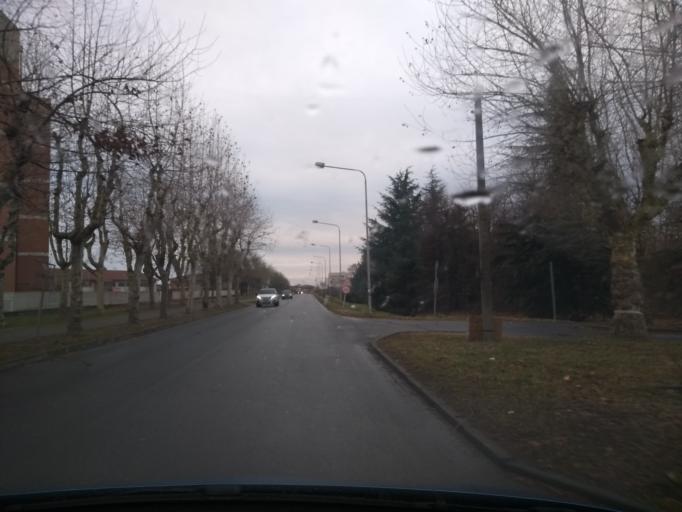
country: IT
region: Piedmont
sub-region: Provincia di Torino
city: Castellamonte
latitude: 45.3811
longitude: 7.7076
